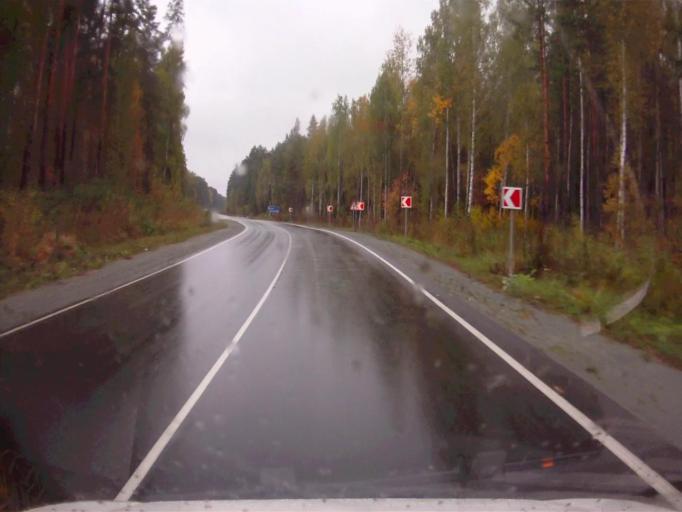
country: RU
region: Chelyabinsk
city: Kyshtym
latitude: 55.6348
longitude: 60.5987
